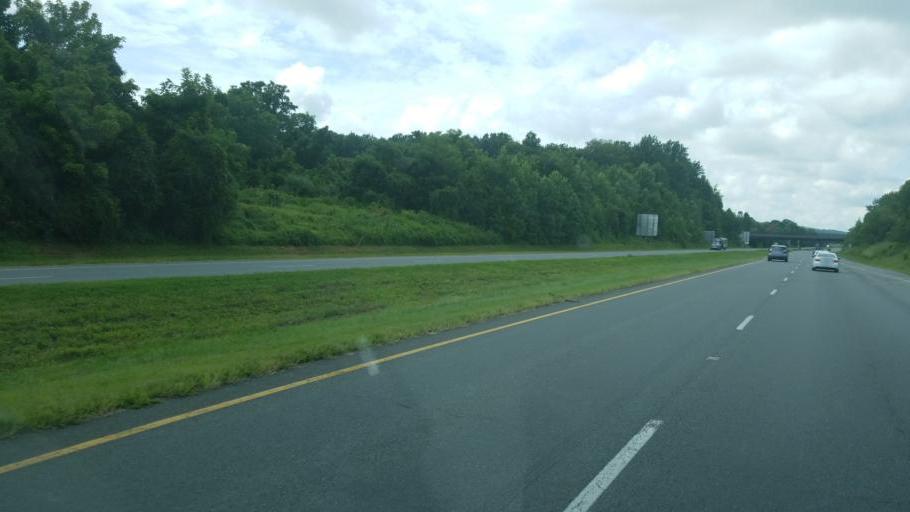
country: US
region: Virginia
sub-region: Fauquier County
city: Warrenton
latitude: 38.7307
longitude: -77.7855
